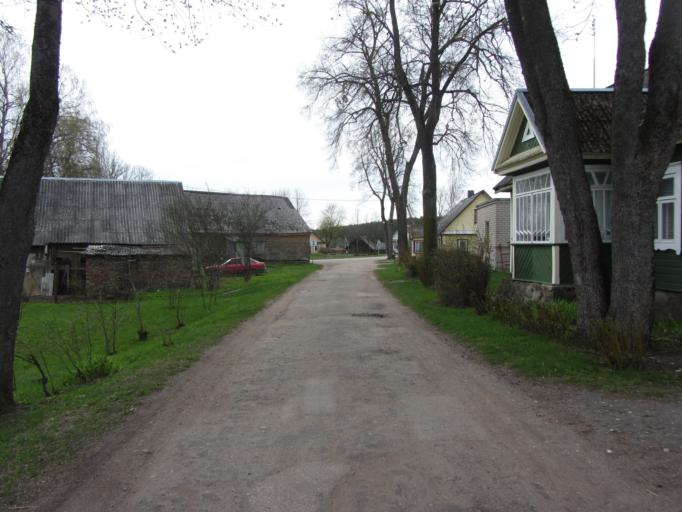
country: LT
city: Zarasai
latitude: 55.5824
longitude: 26.1334
